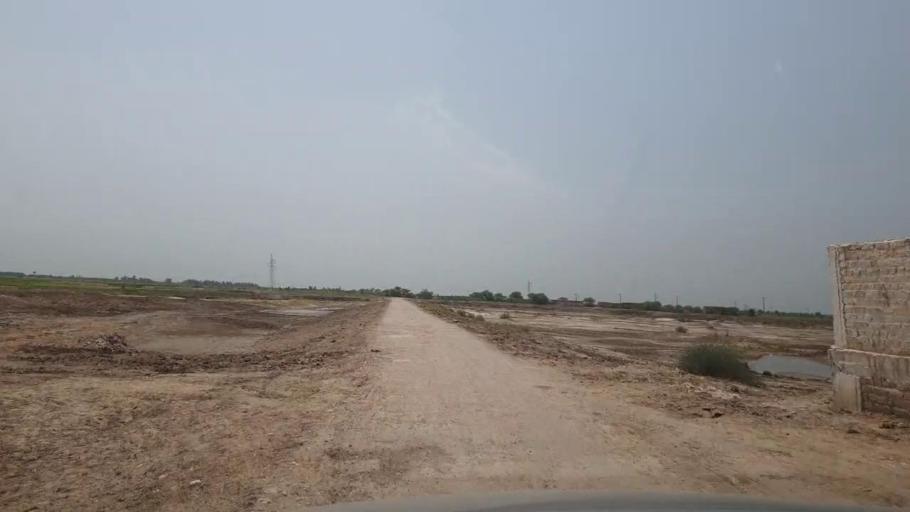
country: PK
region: Sindh
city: Garhi Yasin
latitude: 27.8925
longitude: 68.4934
